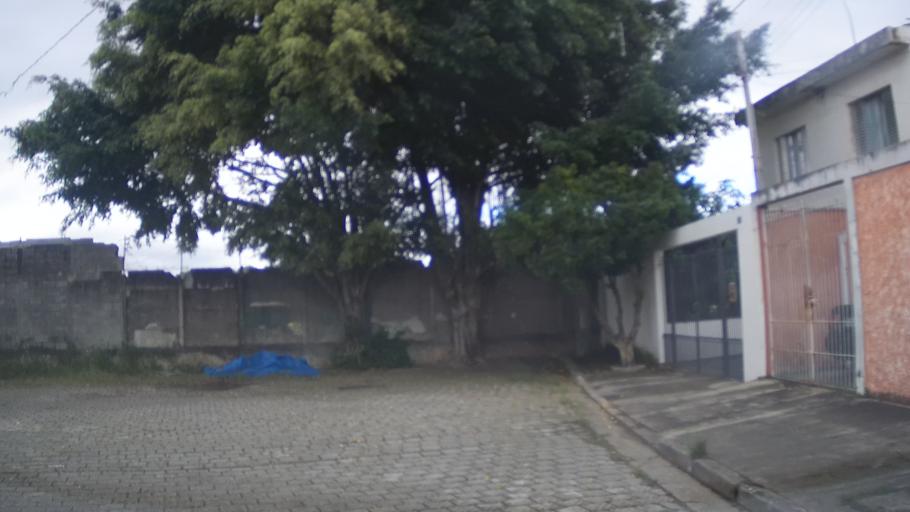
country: BR
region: Sao Paulo
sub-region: Guarulhos
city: Guarulhos
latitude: -23.5021
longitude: -46.5472
